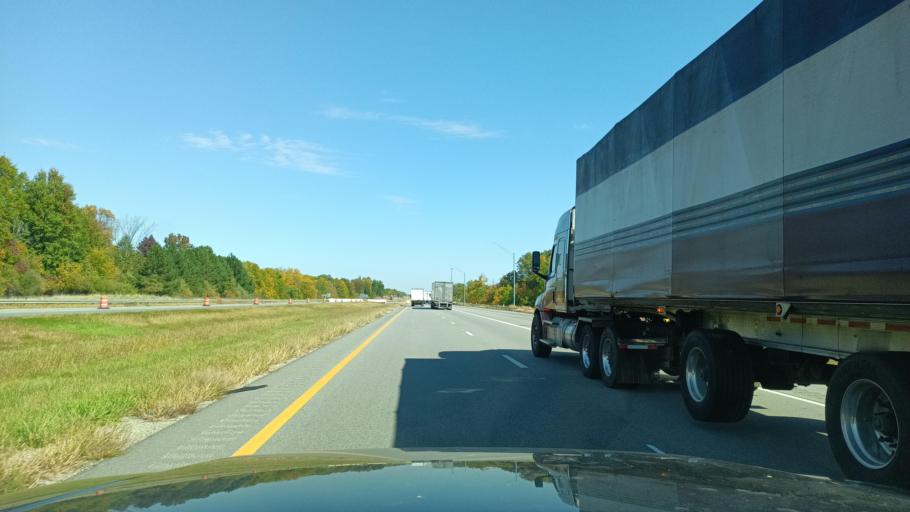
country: US
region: Ohio
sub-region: Defiance County
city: Defiance
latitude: 41.2793
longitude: -84.4113
